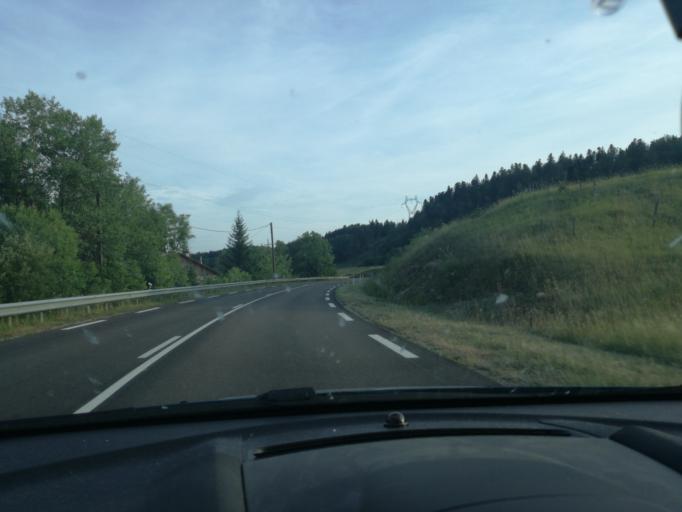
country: FR
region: Franche-Comte
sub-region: Departement du Jura
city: Morbier
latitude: 46.6190
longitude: 5.9598
